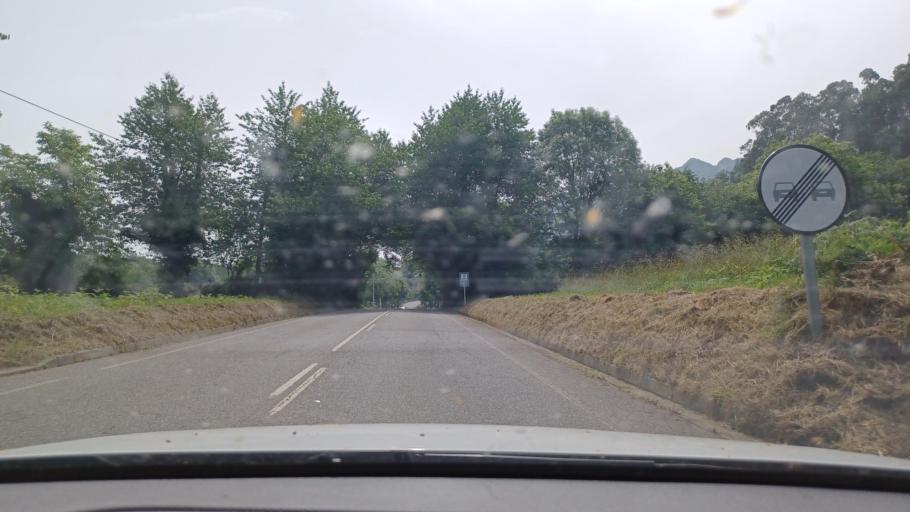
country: ES
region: Asturias
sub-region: Province of Asturias
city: Ribadesella
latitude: 43.4439
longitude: -5.0025
